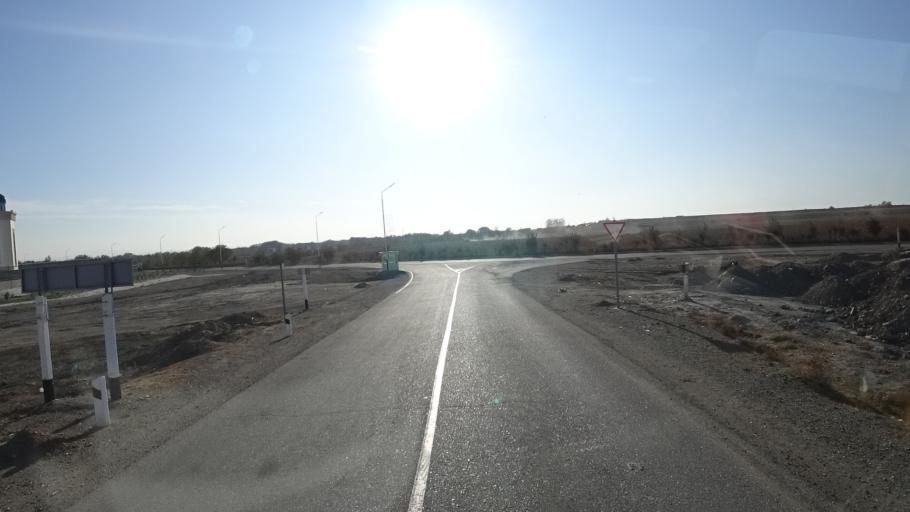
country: UZ
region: Navoiy
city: Beshrabot
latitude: 40.2186
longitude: 65.3837
